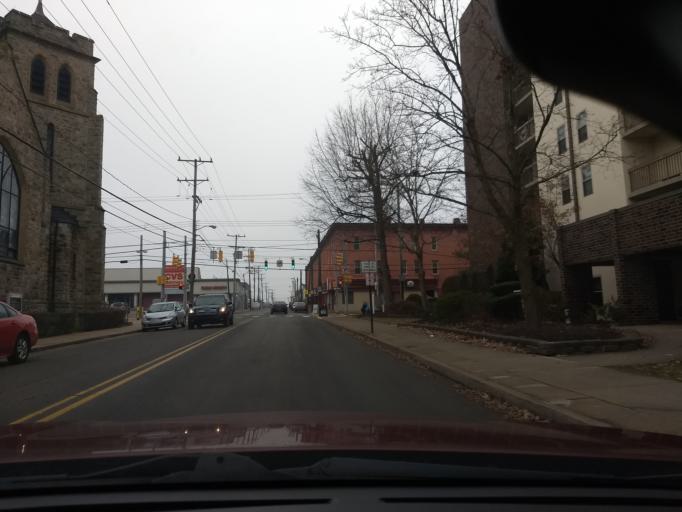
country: US
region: Pennsylvania
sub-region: Allegheny County
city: Swissvale
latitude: 40.4224
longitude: -79.8907
